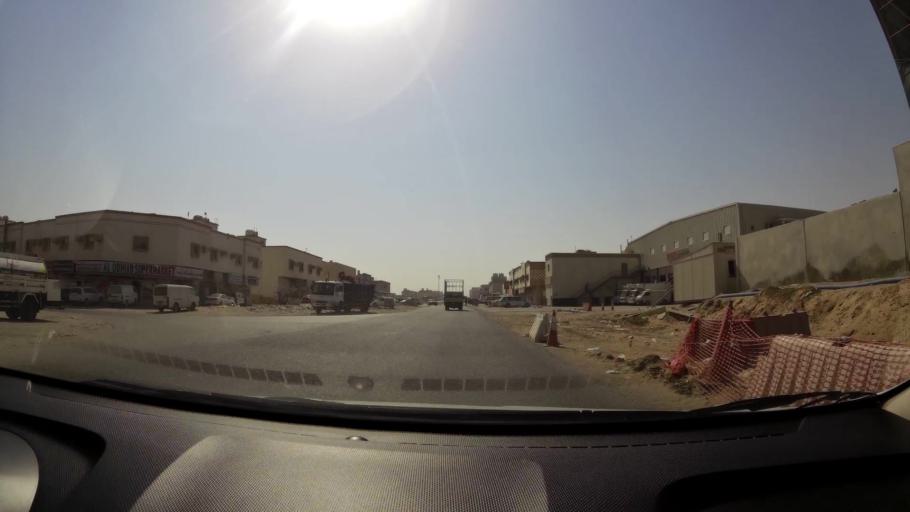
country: AE
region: Ajman
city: Ajman
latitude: 25.4322
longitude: 55.5459
